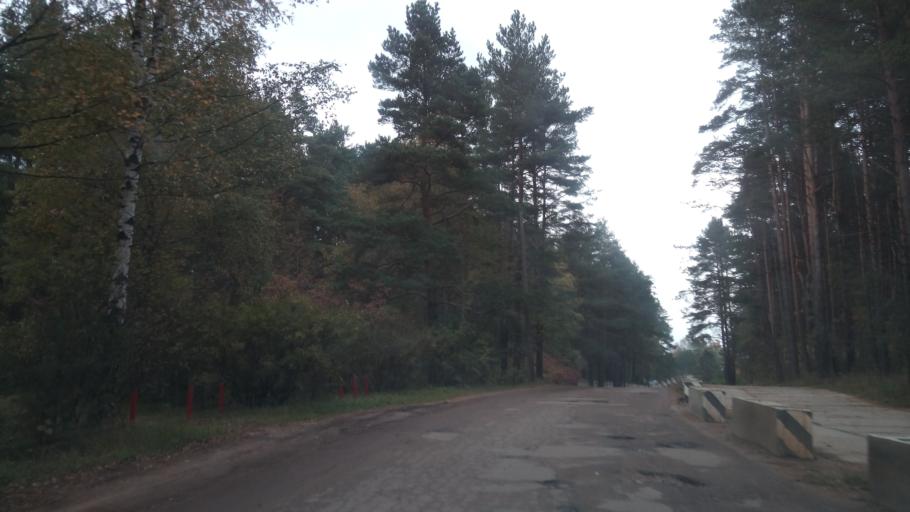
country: BY
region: Minsk
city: Zhdanovichy
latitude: 53.9543
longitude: 27.4383
